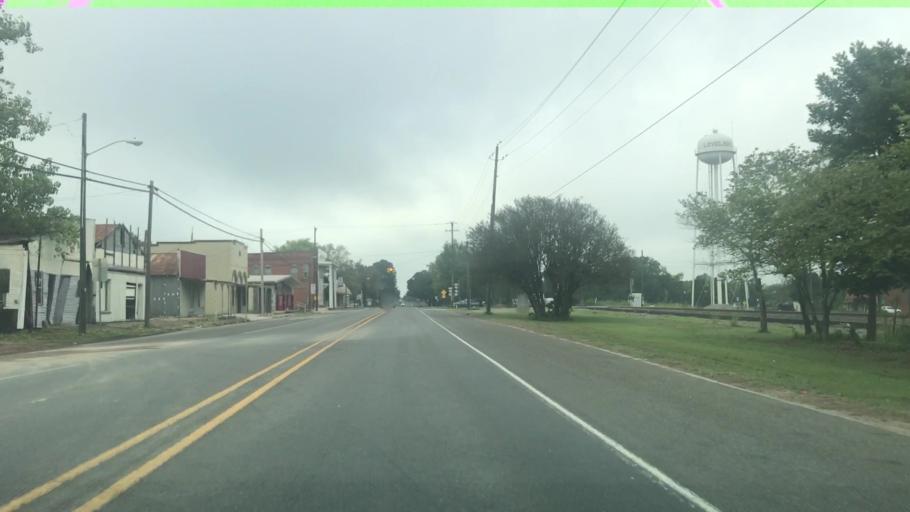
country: US
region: Texas
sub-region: Houston County
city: Cooper
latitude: 31.1279
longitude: -95.4457
